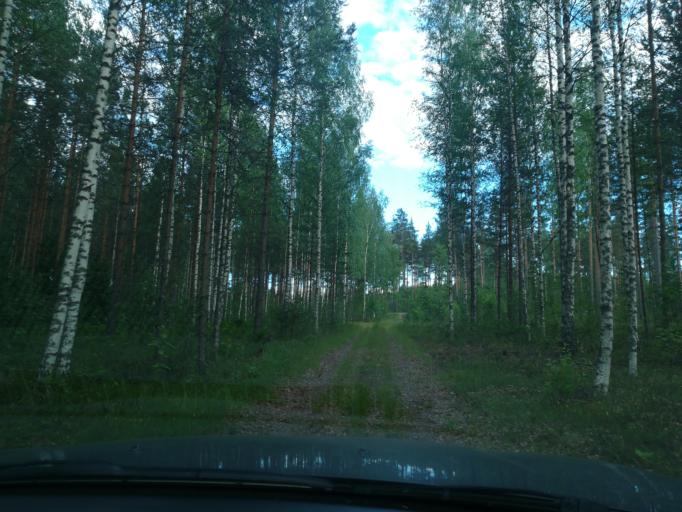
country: FI
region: South Karelia
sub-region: Lappeenranta
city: Savitaipale
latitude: 61.5022
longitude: 27.8382
